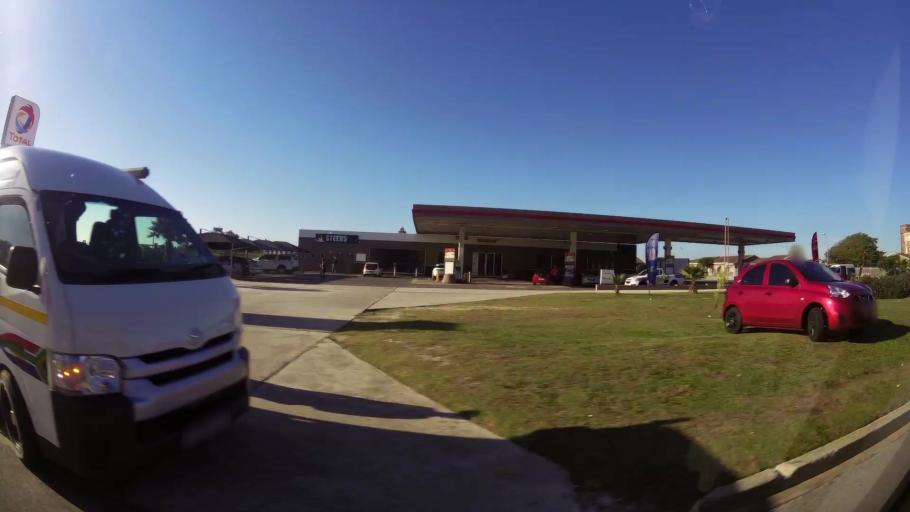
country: ZA
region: Eastern Cape
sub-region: Nelson Mandela Bay Metropolitan Municipality
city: Port Elizabeth
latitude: -33.9924
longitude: 25.6740
